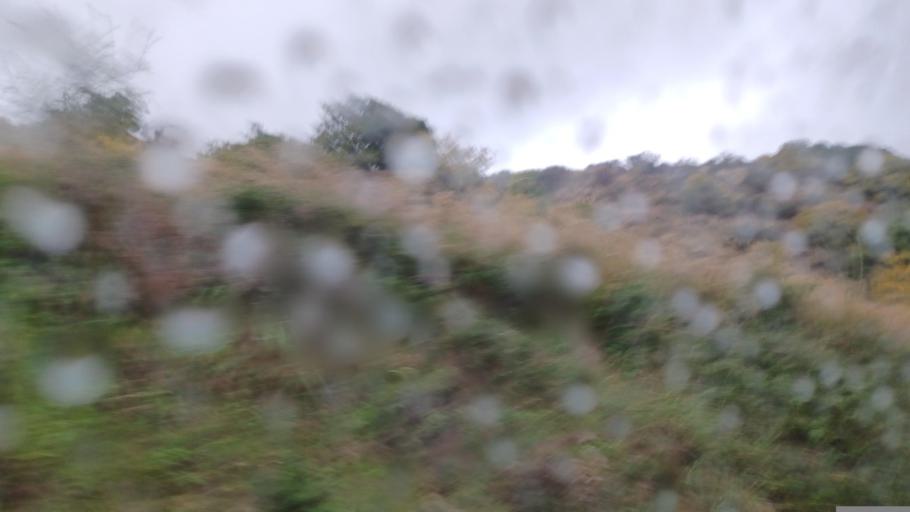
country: CY
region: Pafos
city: Mesogi
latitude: 34.8719
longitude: 32.5399
